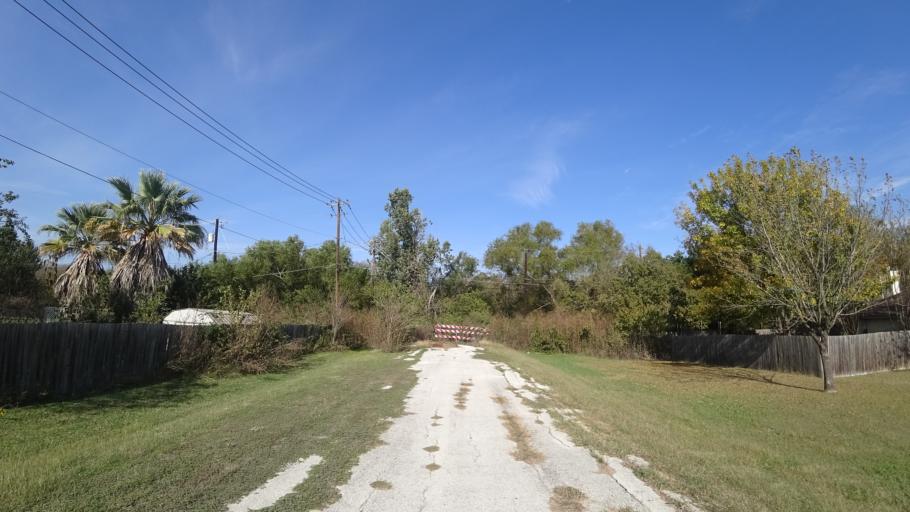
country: US
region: Texas
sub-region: Travis County
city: Pflugerville
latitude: 30.4249
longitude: -97.6309
